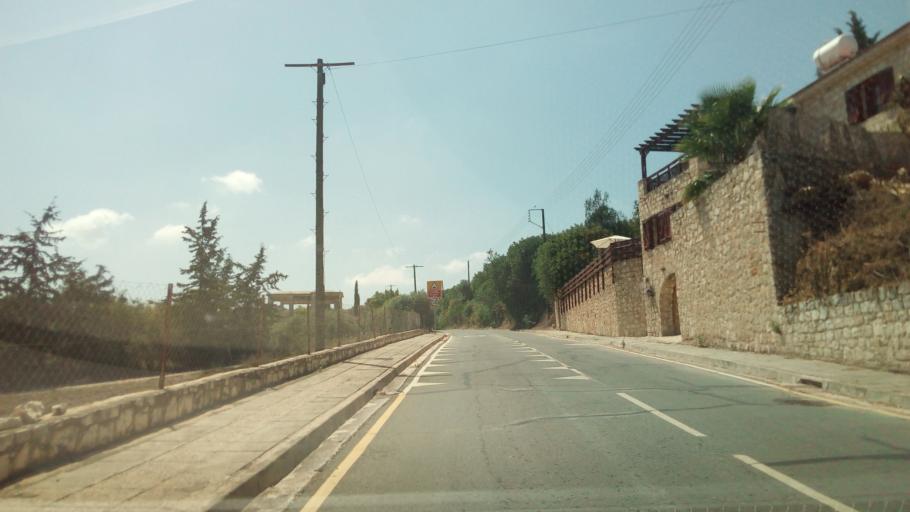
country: CY
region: Pafos
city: Polis
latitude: 34.9434
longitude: 32.5024
